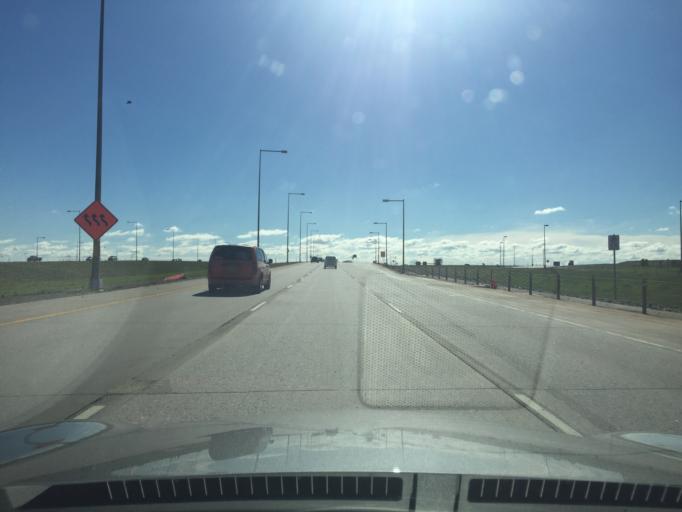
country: US
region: Colorado
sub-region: Adams County
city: Aurora
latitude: 39.8335
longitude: -104.6998
